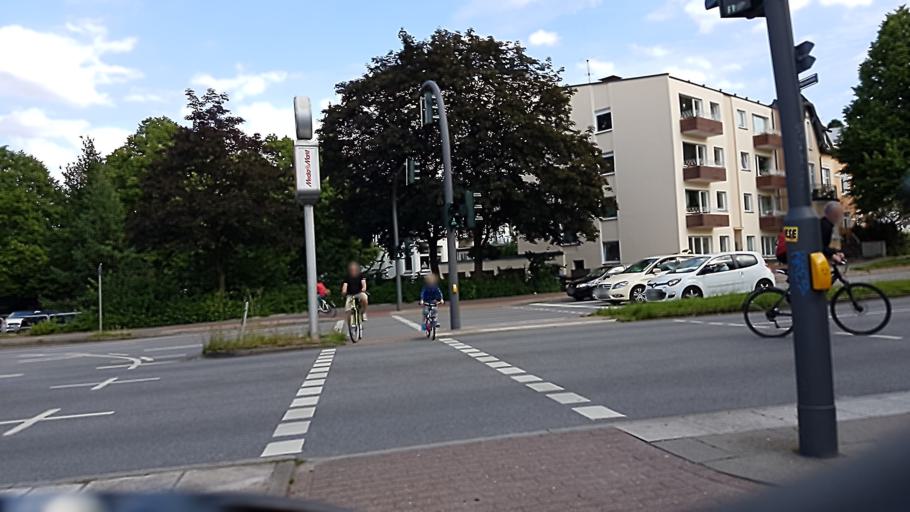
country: DE
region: Hamburg
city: Hamburg-Nord
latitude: 53.6010
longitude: 9.9839
